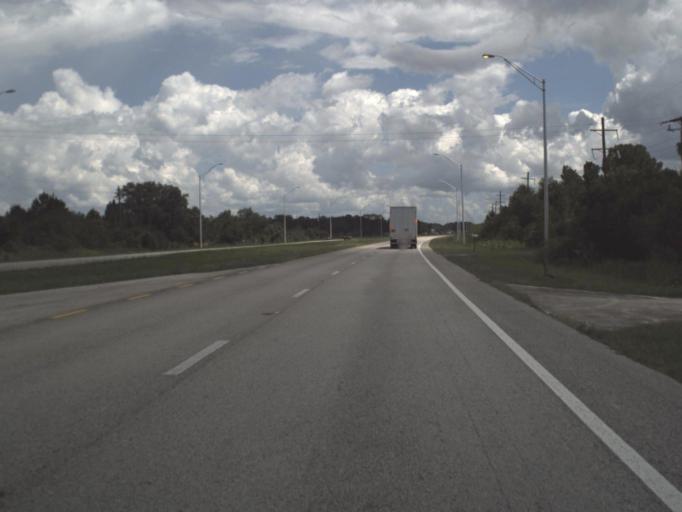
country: US
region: Florida
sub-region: Polk County
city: Babson Park
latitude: 27.8772
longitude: -81.4099
